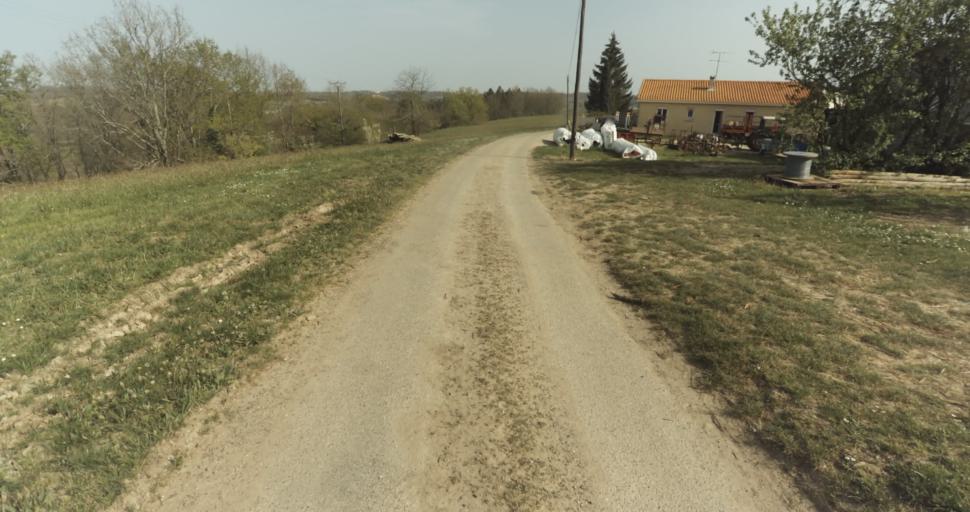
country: FR
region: Midi-Pyrenees
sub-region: Departement du Tarn-et-Garonne
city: Lafrancaise
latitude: 44.1509
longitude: 1.1680
